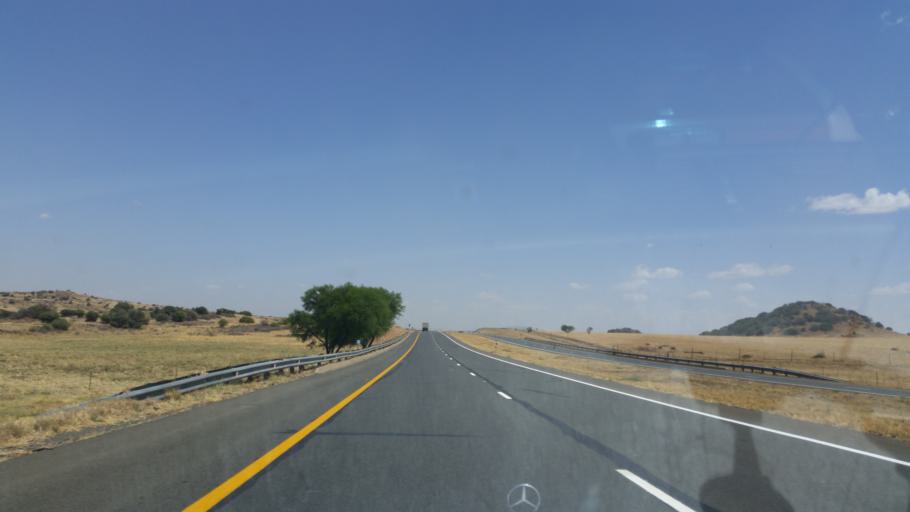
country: ZA
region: Orange Free State
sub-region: Lejweleputswa District Municipality
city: Brandfort
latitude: -28.9268
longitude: 26.4318
